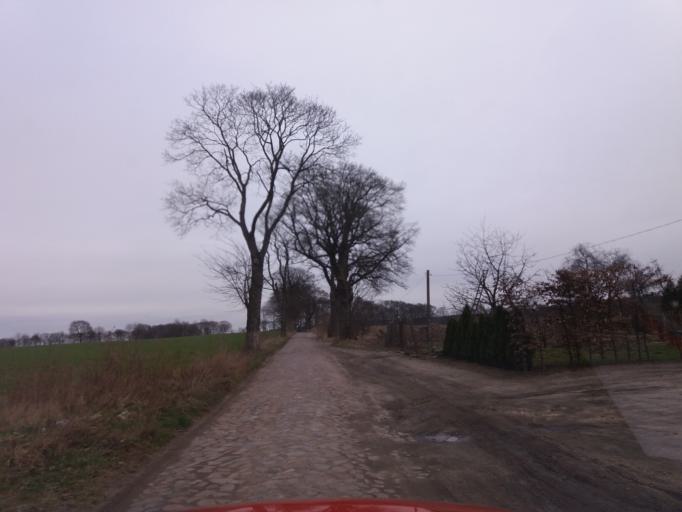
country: PL
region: West Pomeranian Voivodeship
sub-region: Powiat choszczenski
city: Recz
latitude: 53.1599
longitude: 15.6098
